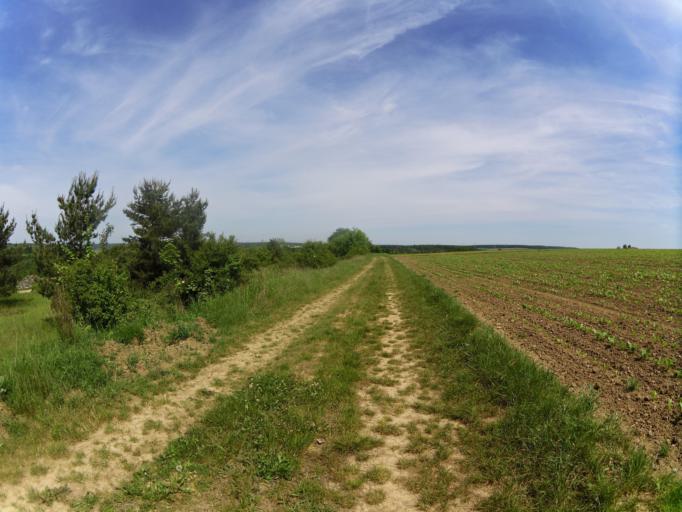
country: DE
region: Bavaria
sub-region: Regierungsbezirk Unterfranken
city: Sommerhausen
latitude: 49.6724
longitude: 10.0236
